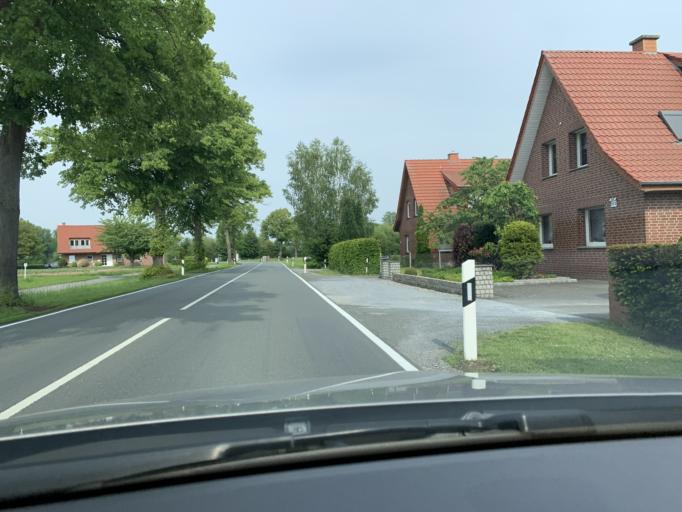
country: DE
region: North Rhine-Westphalia
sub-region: Regierungsbezirk Detmold
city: Langenberg
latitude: 51.7786
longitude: 8.3513
